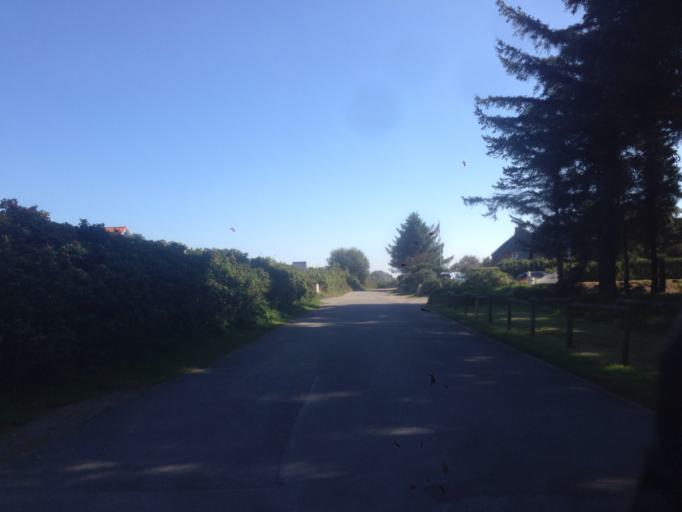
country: DE
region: Schleswig-Holstein
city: Westerland
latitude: 54.9417
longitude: 8.3281
